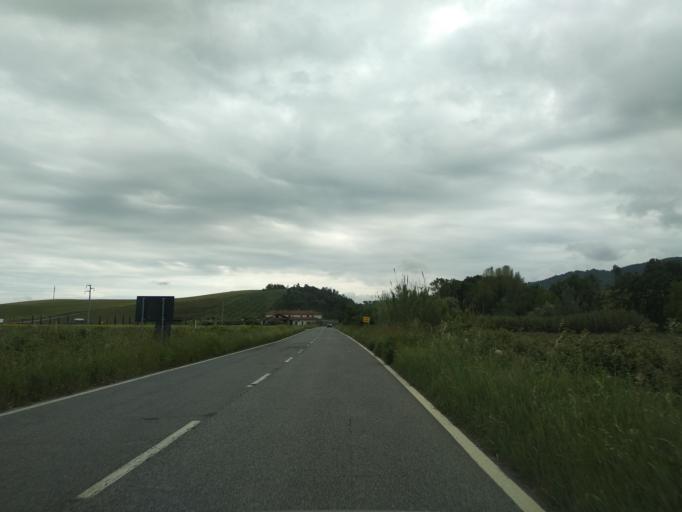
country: IT
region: Tuscany
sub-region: Provincia di Livorno
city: Collesalvetti
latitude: 43.5374
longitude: 10.4631
